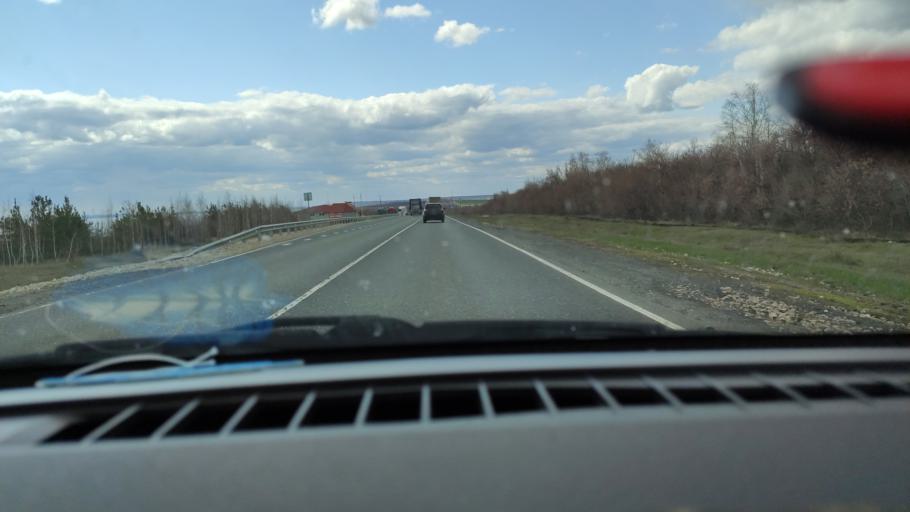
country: RU
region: Saratov
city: Balakovo
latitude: 52.1570
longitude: 47.8178
